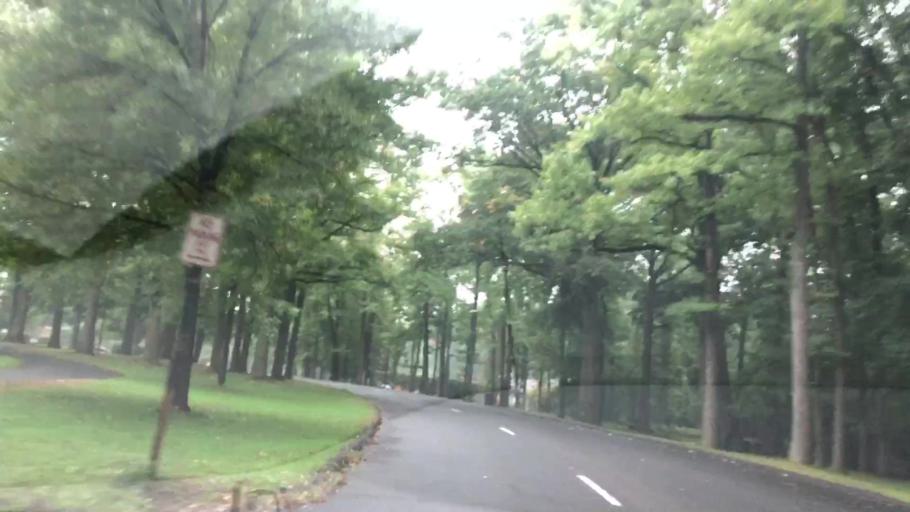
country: US
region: New Jersey
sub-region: Union County
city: Rahway
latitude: 40.6227
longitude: -74.2890
